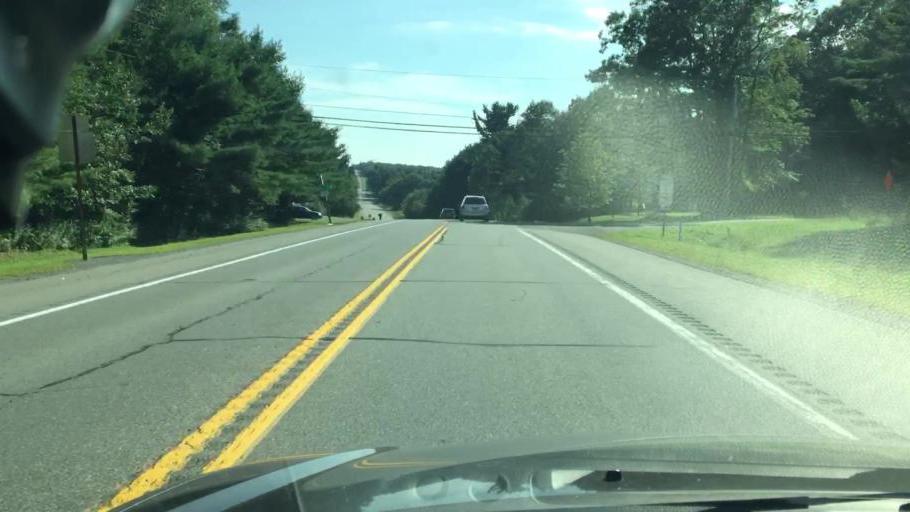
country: US
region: Pennsylvania
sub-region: Carbon County
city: Towamensing Trails
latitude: 40.9689
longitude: -75.6442
